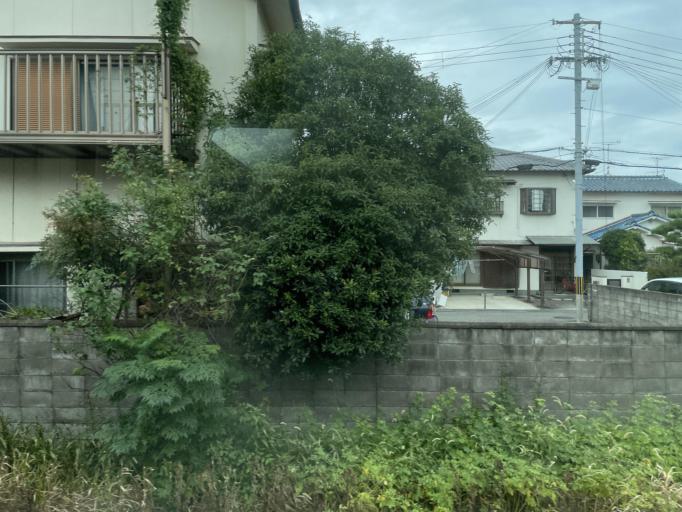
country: JP
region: Wakayama
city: Wakayama-shi
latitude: 34.2477
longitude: 135.2008
